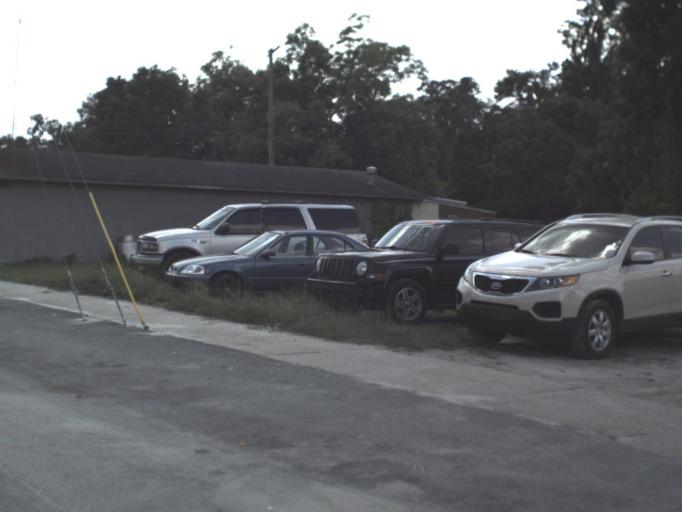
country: US
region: Georgia
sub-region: Echols County
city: Statenville
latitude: 30.6037
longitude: -83.0985
